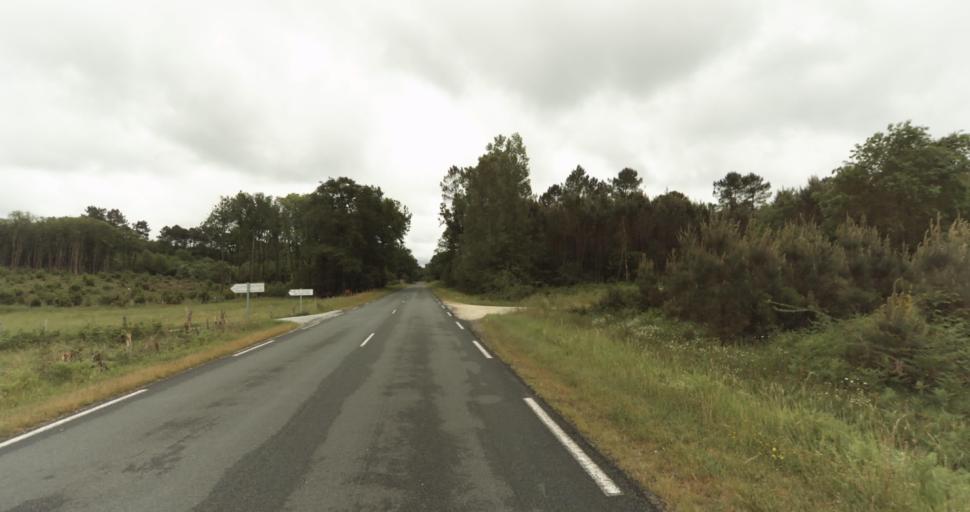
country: FR
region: Aquitaine
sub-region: Departement de la Dordogne
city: Belves
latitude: 44.6837
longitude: 0.9902
